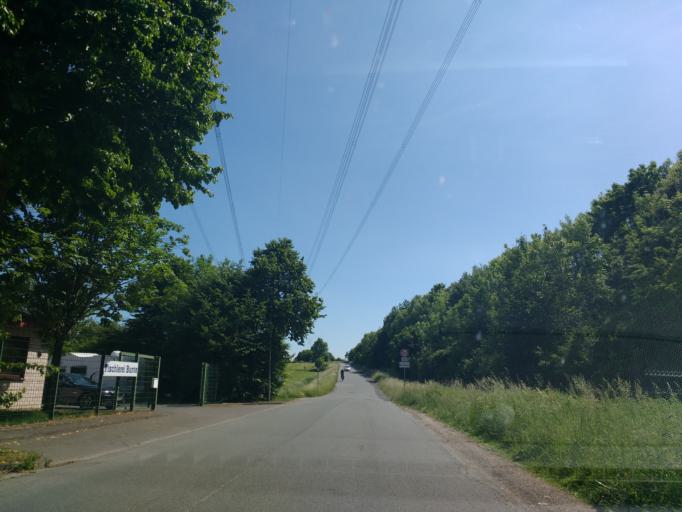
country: DE
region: North Rhine-Westphalia
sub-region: Regierungsbezirk Detmold
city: Paderborn
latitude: 51.6934
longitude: 8.7103
